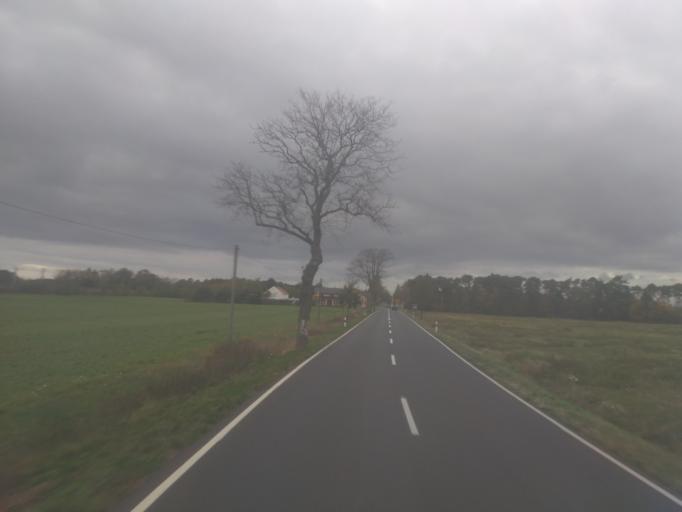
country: DE
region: Brandenburg
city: Merzdorf
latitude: 51.4057
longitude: 13.4970
